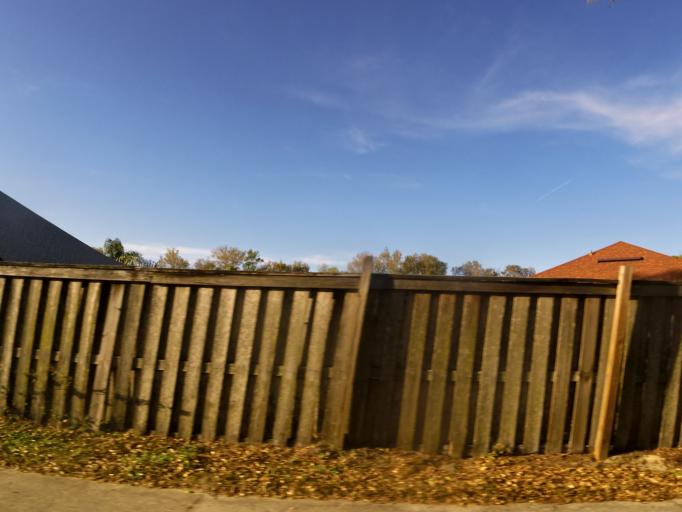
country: US
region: Florida
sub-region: Duval County
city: Jacksonville
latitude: 30.4399
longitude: -81.6177
